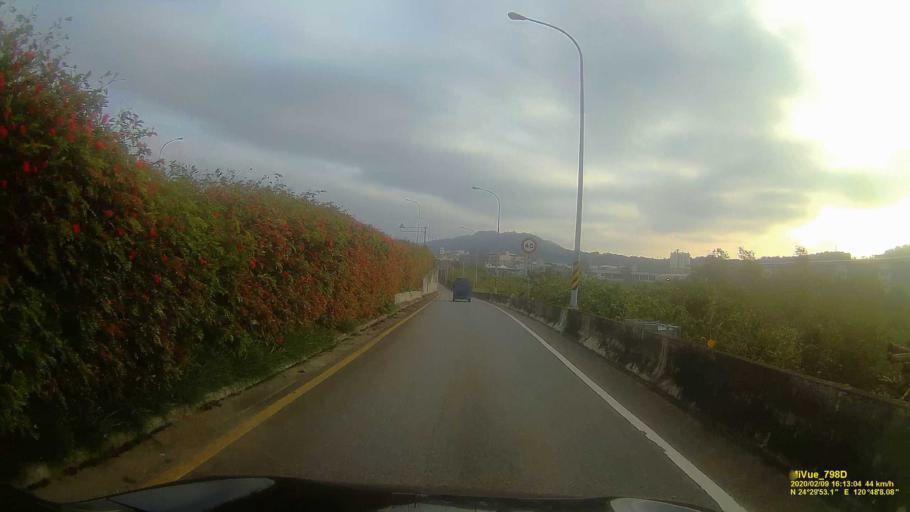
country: TW
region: Taiwan
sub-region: Miaoli
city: Miaoli
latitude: 24.4979
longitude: 120.8022
